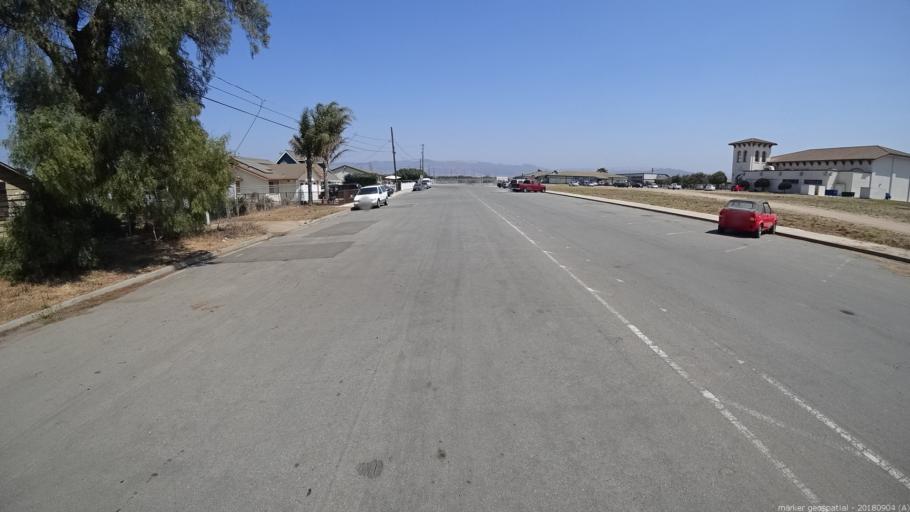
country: US
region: California
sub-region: Monterey County
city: Chualar
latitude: 36.5720
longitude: -121.5183
